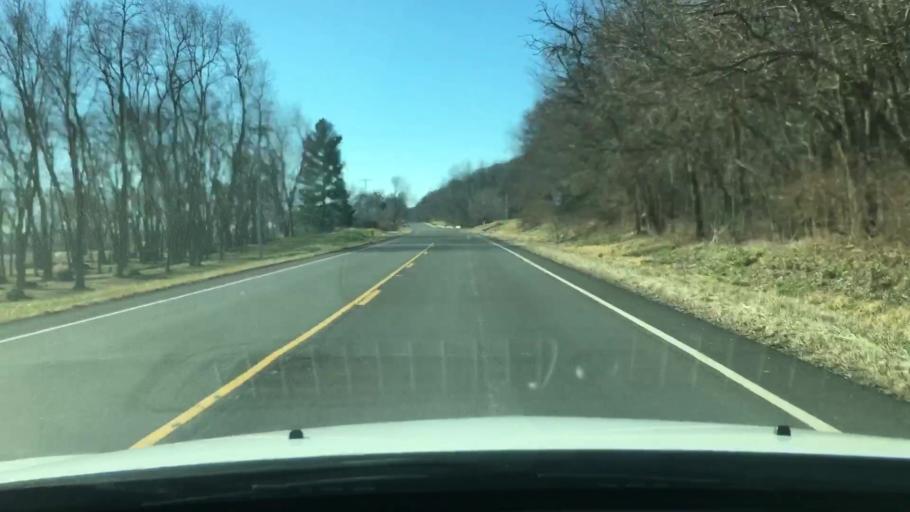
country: US
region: Illinois
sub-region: Mason County
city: Havana
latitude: 40.4164
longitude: -90.0129
